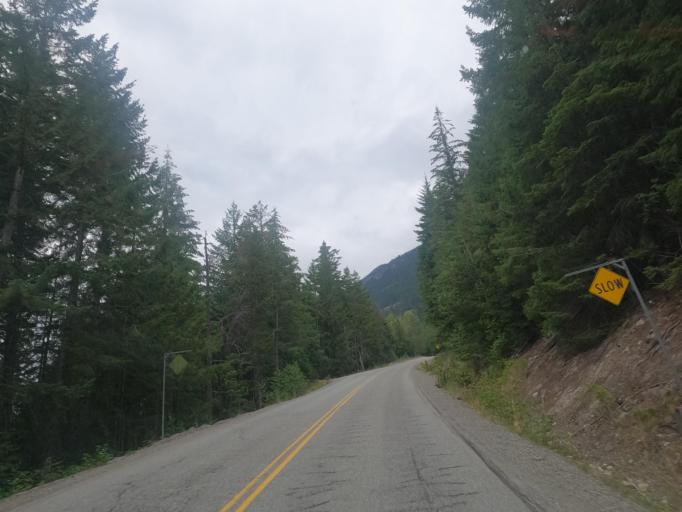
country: CA
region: British Columbia
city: Pemberton
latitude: 50.3016
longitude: -122.5845
